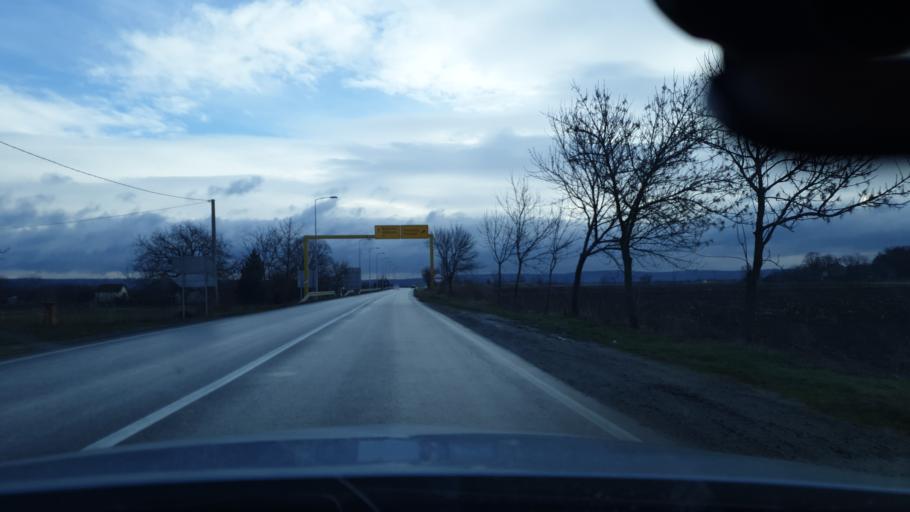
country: RS
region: Central Serbia
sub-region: Branicevski Okrug
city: Pozarevac
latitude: 44.6014
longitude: 21.1425
